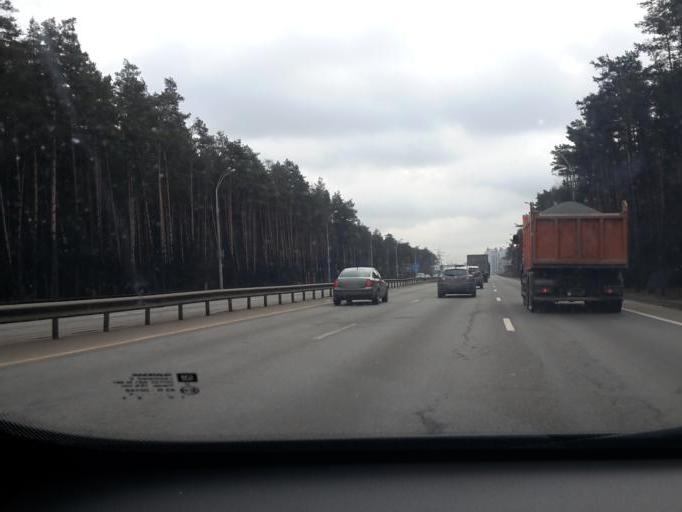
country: BY
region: Minsk
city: Borovlyany
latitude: 53.9494
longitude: 27.6554
